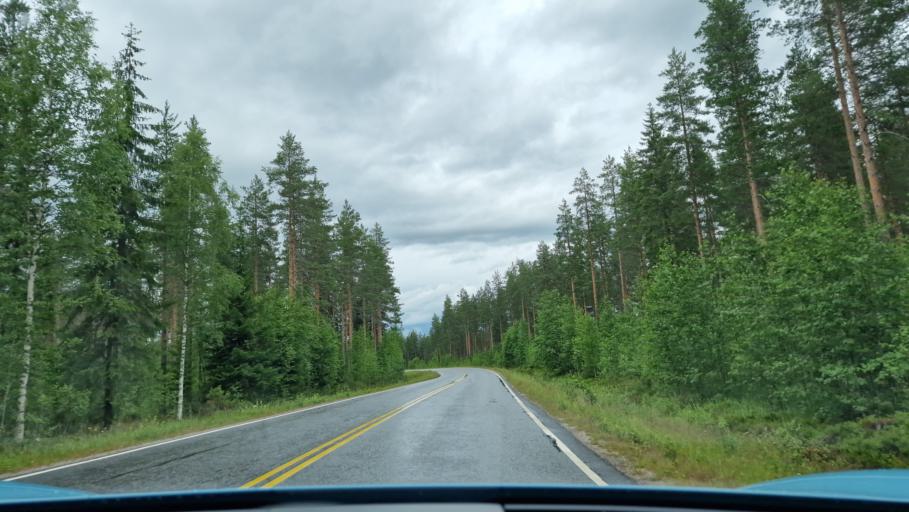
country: FI
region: Southern Ostrobothnia
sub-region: Jaerviseutu
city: Soini
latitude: 62.6861
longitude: 24.4685
